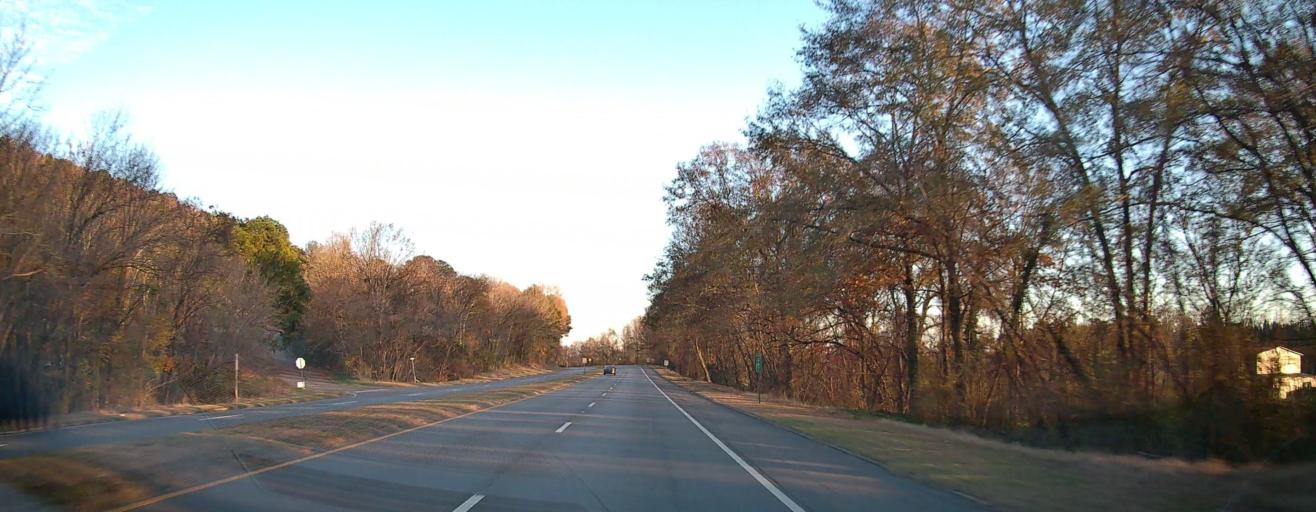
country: US
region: Alabama
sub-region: Etowah County
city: Attalla
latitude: 34.0205
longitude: -86.1027
